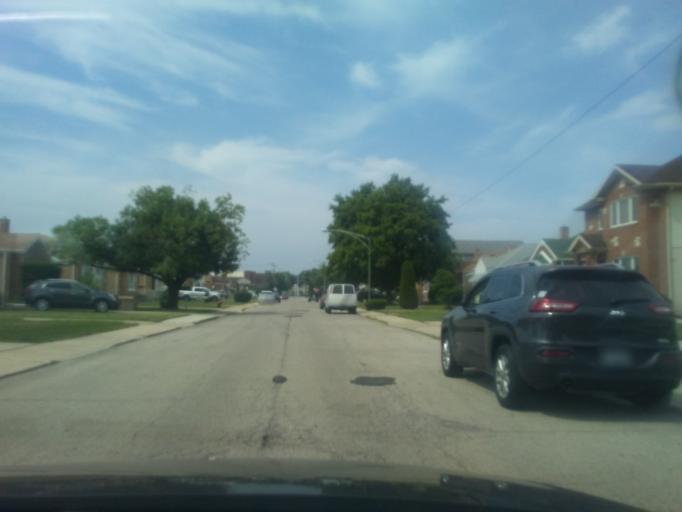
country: US
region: Illinois
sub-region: Cook County
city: Harwood Heights
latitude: 41.9724
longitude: -87.8059
